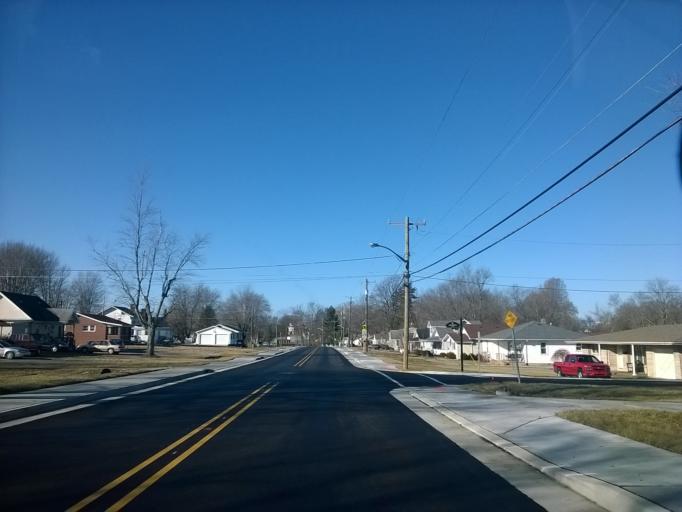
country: US
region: Indiana
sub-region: Scott County
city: Austin
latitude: 38.7433
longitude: -85.7985
